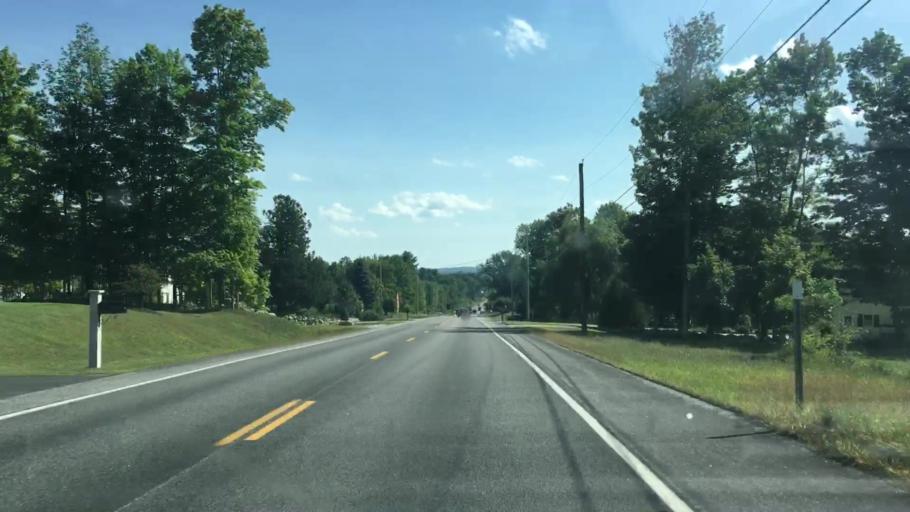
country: US
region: Maine
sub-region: Androscoggin County
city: Lisbon Falls
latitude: 44.0273
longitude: -70.0675
